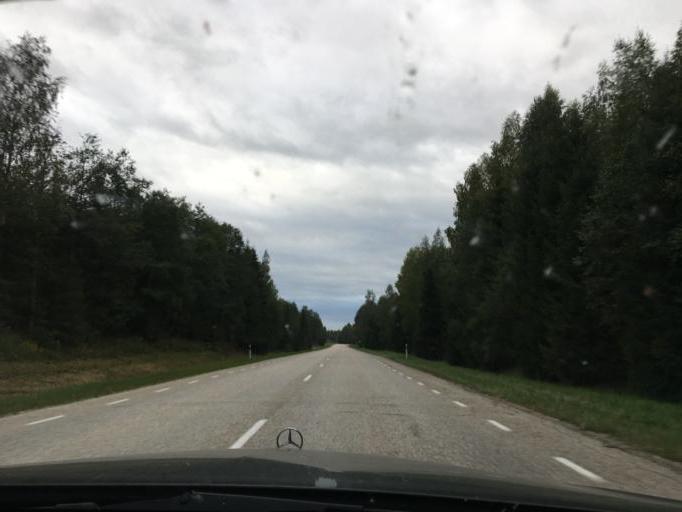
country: LV
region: Aluksnes Rajons
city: Aluksne
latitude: 57.6289
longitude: 27.3023
